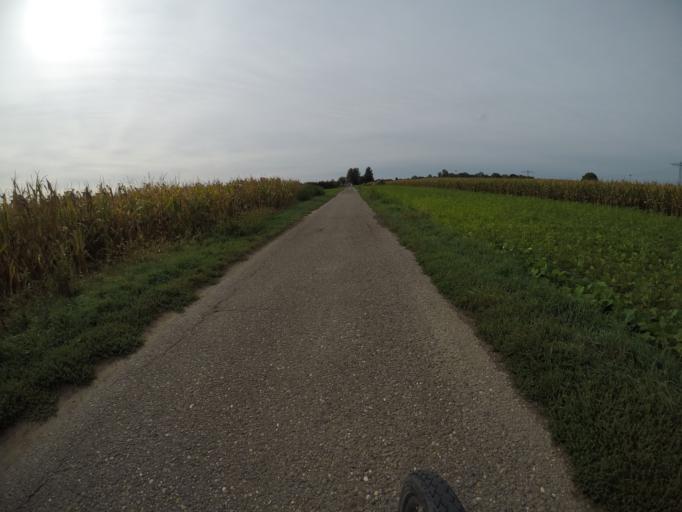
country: DE
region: Baden-Wuerttemberg
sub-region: Karlsruhe Region
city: Kronau
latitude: 49.2311
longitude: 8.6301
